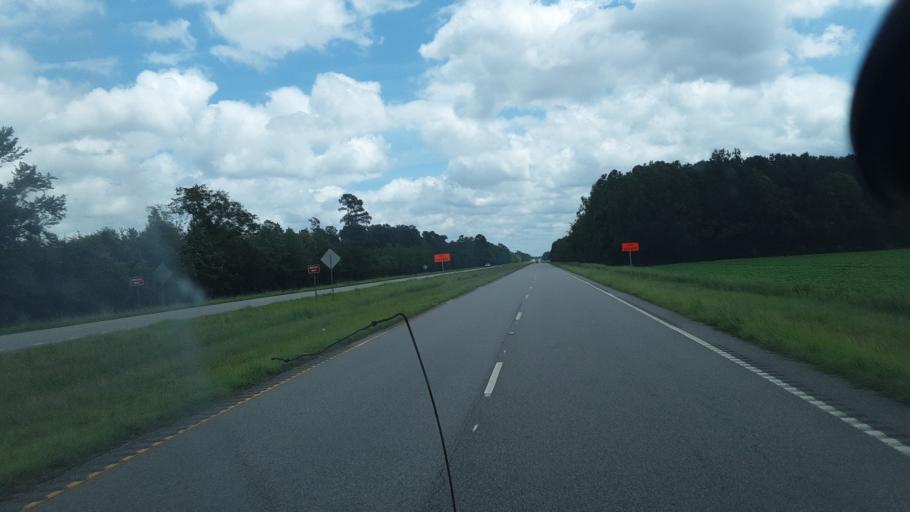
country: US
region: South Carolina
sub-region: Horry County
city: Loris
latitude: 34.0929
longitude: -78.9067
